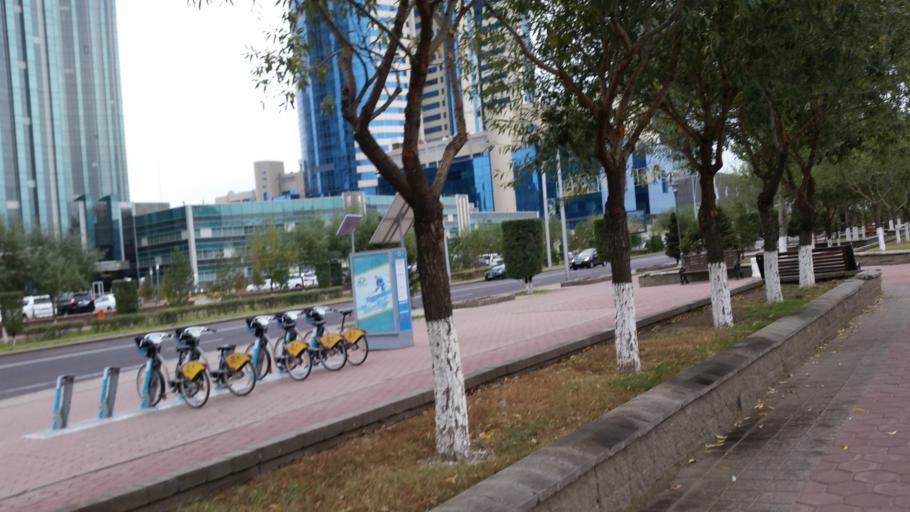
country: KZ
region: Astana Qalasy
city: Astana
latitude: 51.1318
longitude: 71.4247
